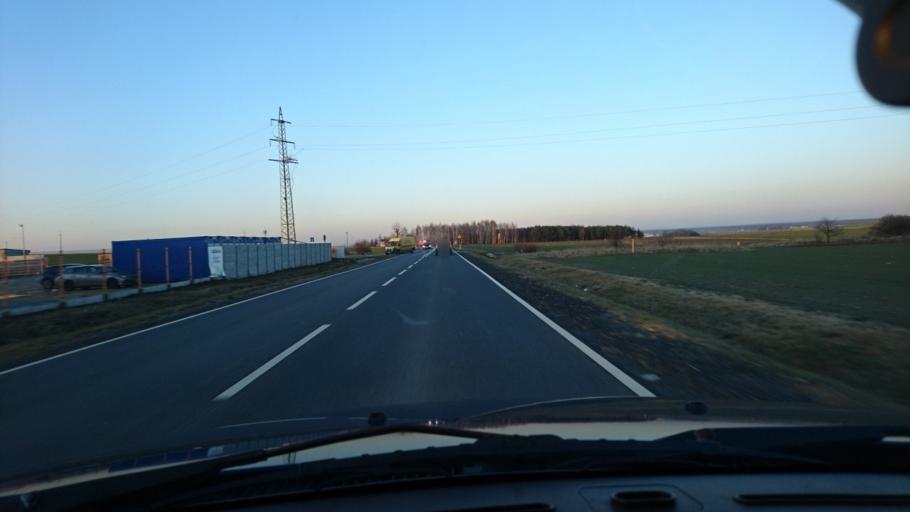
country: PL
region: Silesian Voivodeship
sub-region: Powiat gliwicki
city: Wielowies
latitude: 50.4906
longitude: 18.6066
